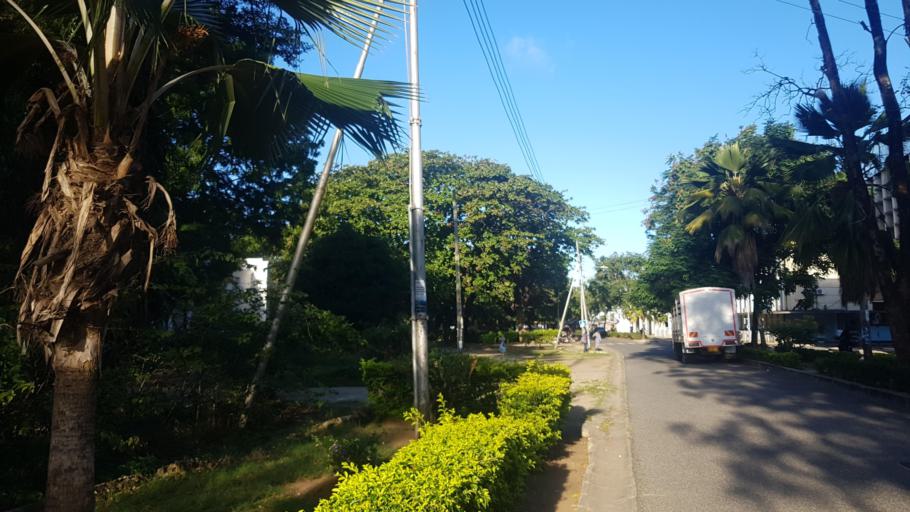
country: TZ
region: Tanga
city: Tanga
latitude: -5.0696
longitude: 39.0983
